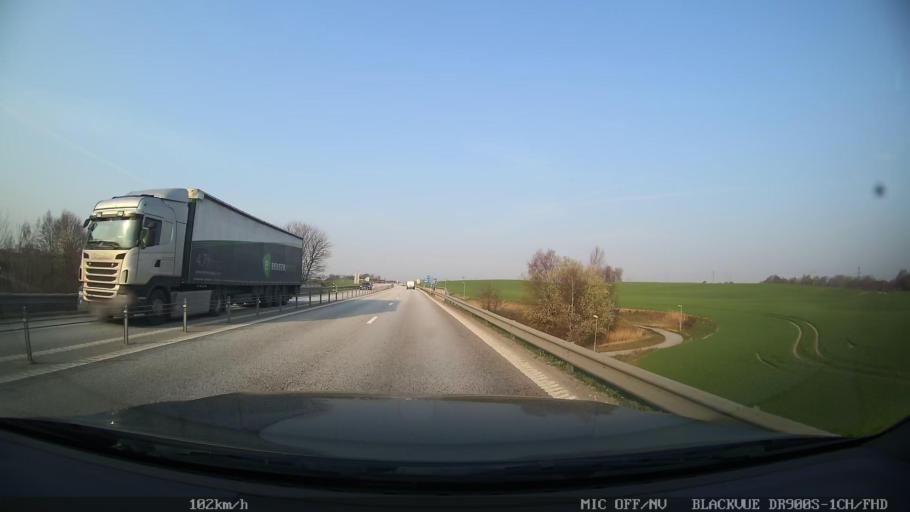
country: SE
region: Skane
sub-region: Skurups Kommun
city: Skurup
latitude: 55.4948
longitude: 13.4901
